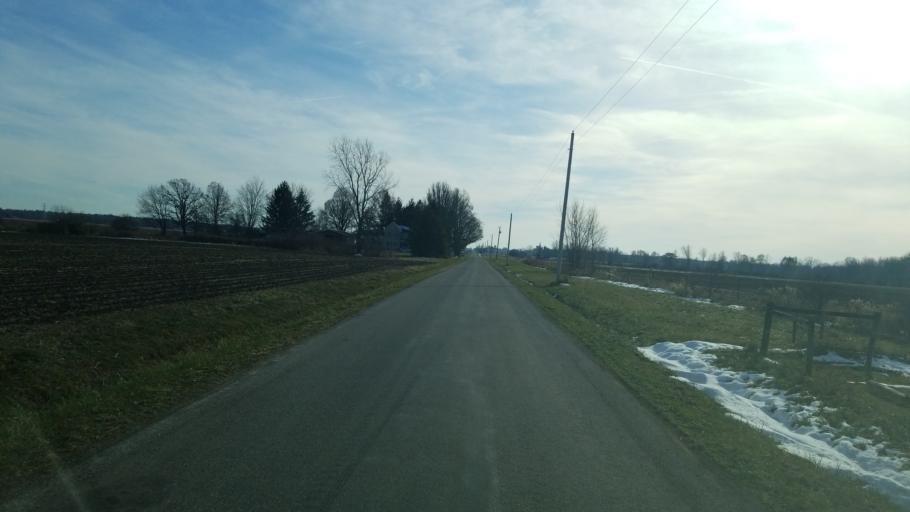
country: US
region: Ohio
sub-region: Huron County
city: New London
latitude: 41.0426
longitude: -82.2801
